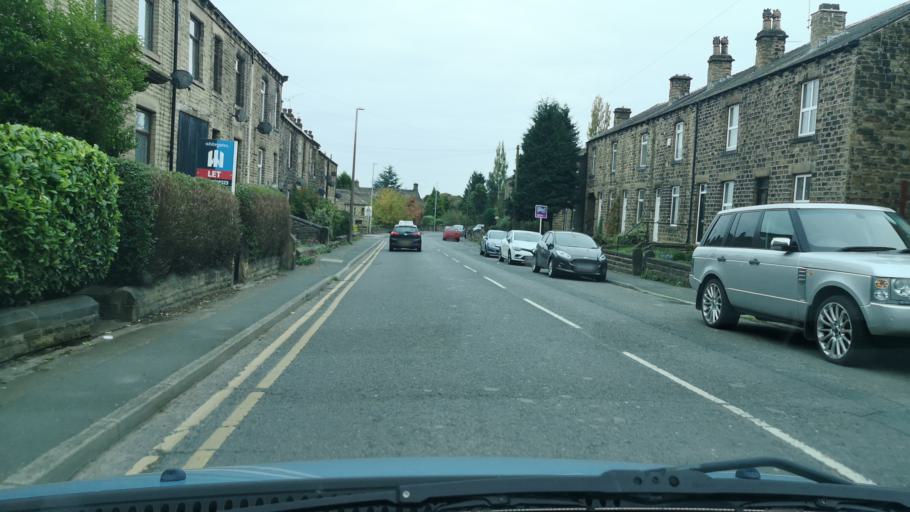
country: GB
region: England
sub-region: Kirklees
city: Dewsbury
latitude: 53.6703
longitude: -1.6218
